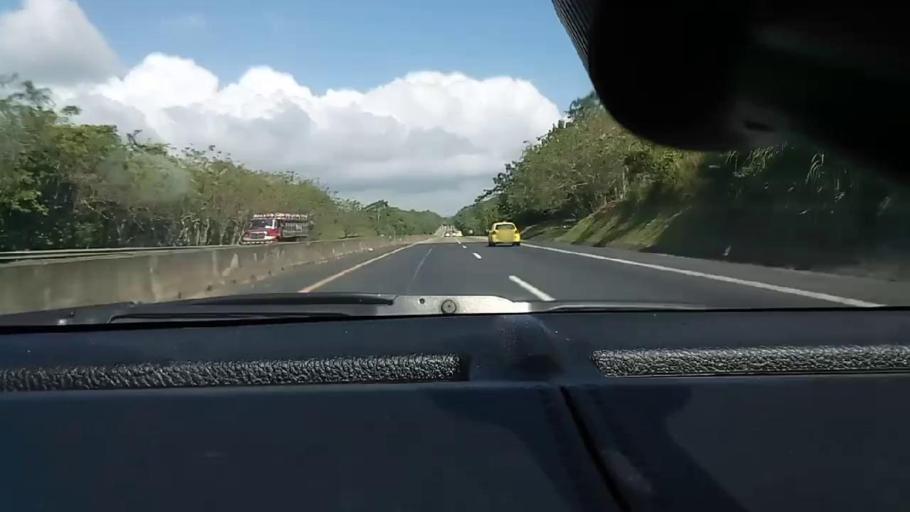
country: PA
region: Panama
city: Alcalde Diaz
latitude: 9.0919
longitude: -79.6027
